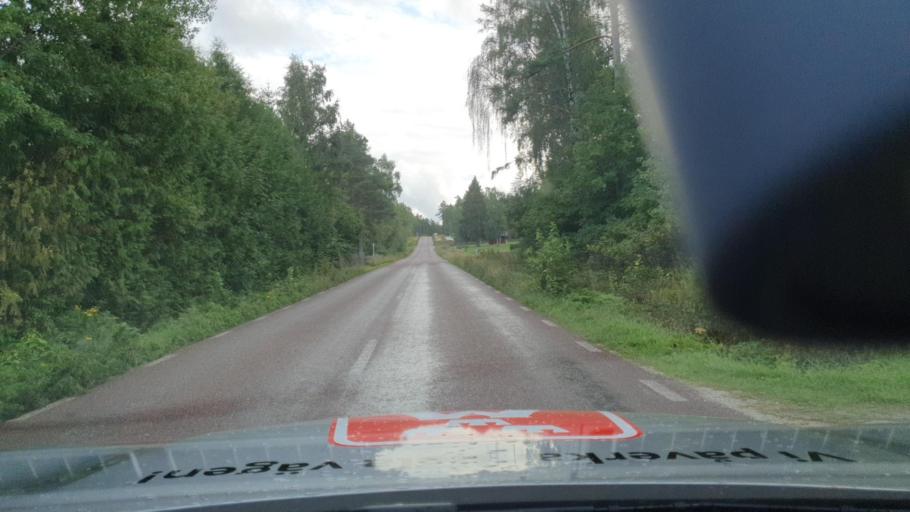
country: SE
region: Gotland
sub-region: Gotland
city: Slite
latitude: 57.6228
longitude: 18.7595
